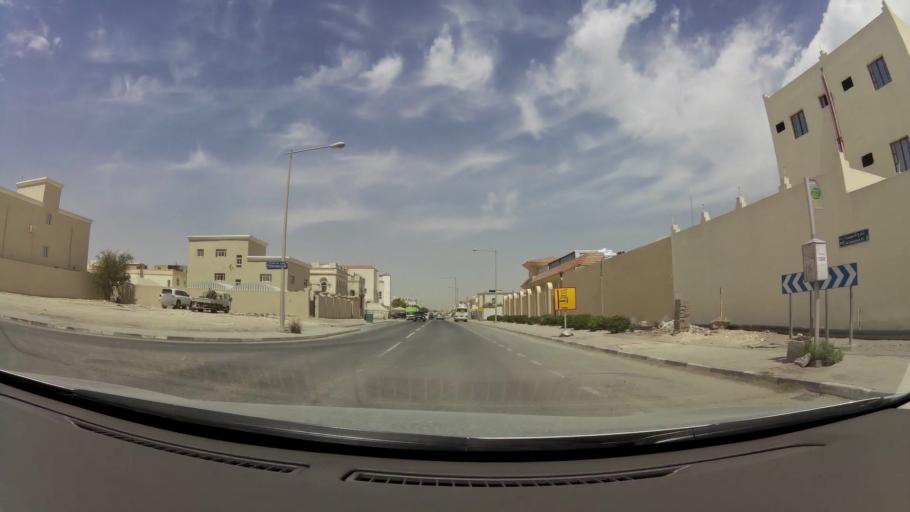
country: QA
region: Baladiyat ar Rayyan
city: Ar Rayyan
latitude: 25.2641
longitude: 51.4264
